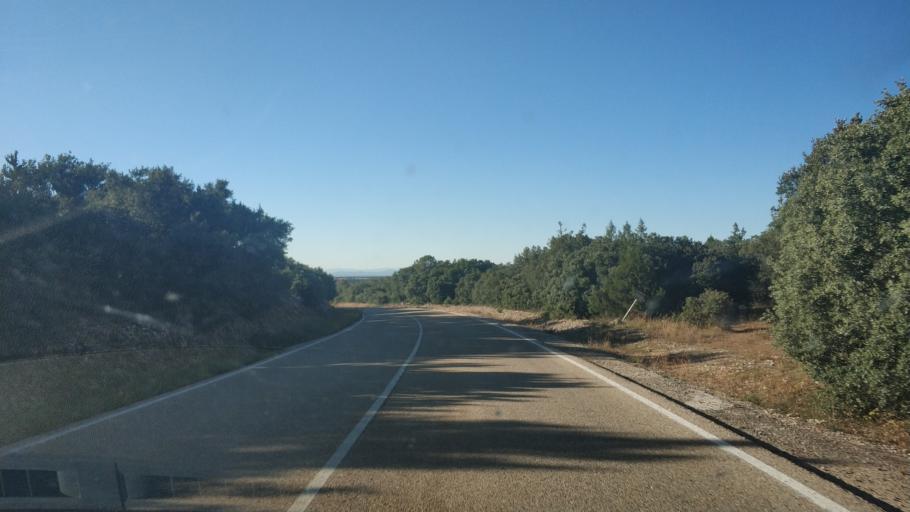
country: ES
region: Castille and Leon
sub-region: Provincia de Soria
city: Montejo de Tiermes
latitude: 41.4112
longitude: -3.2010
